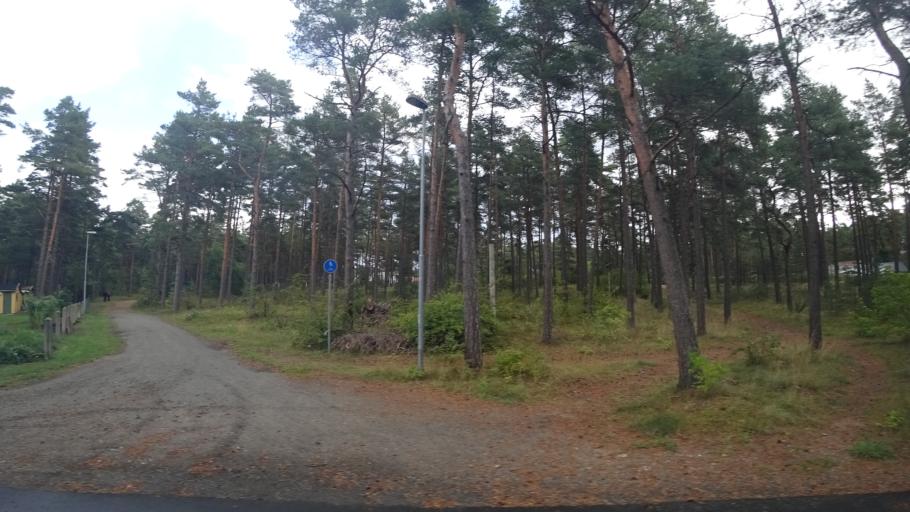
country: SE
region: Skane
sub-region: Kristianstads Kommun
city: Ahus
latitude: 55.9399
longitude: 14.3004
